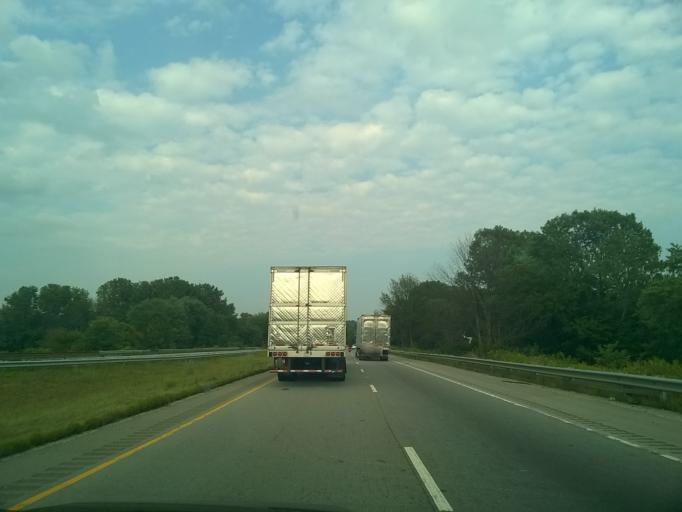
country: US
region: Indiana
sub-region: Putnam County
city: Cloverdale
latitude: 39.5025
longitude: -86.9574
